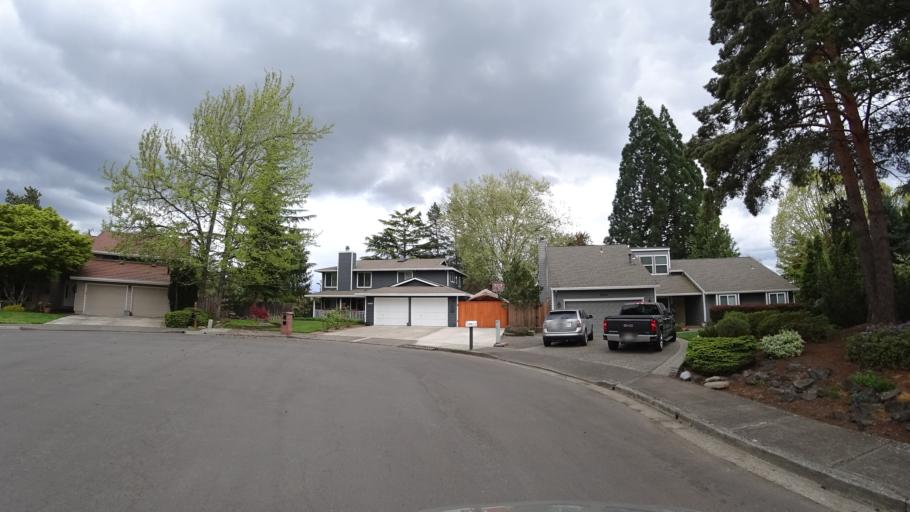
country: US
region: Oregon
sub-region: Washington County
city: Rockcreek
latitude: 45.5536
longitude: -122.8804
